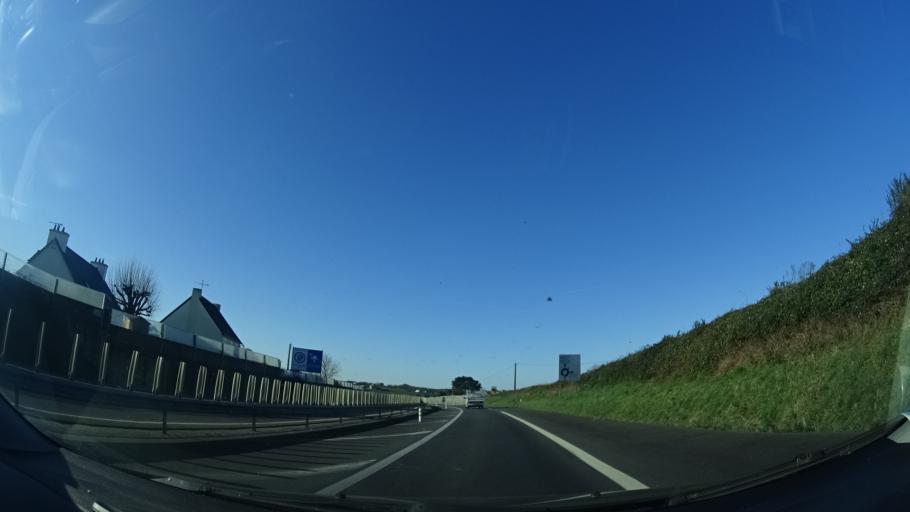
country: FR
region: Brittany
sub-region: Departement du Finistere
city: Henvic
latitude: 48.6453
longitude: -3.9424
